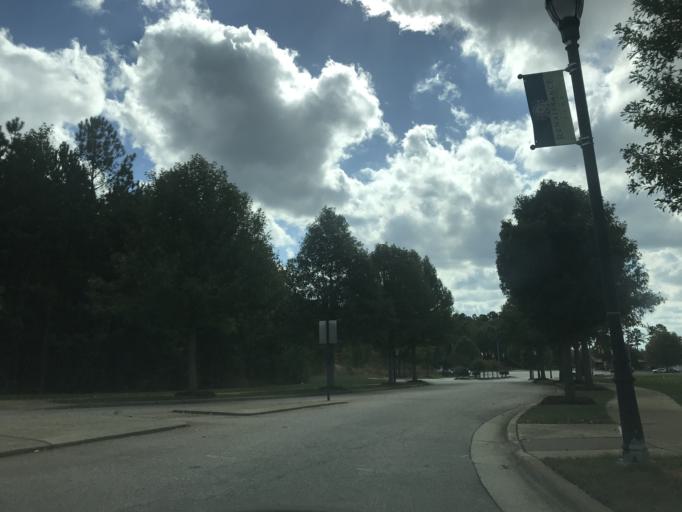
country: US
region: North Carolina
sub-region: Wake County
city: Raleigh
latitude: 35.7339
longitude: -78.6566
